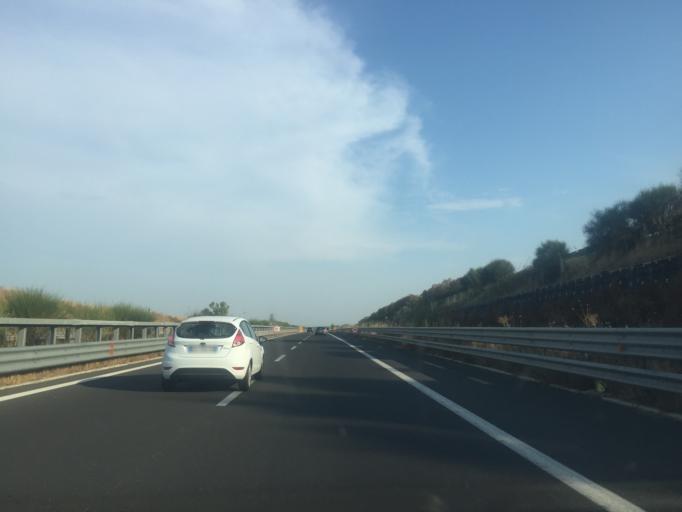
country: IT
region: Sicily
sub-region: Provincia di Siracusa
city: Villasmundo
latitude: 37.2737
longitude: 15.1276
